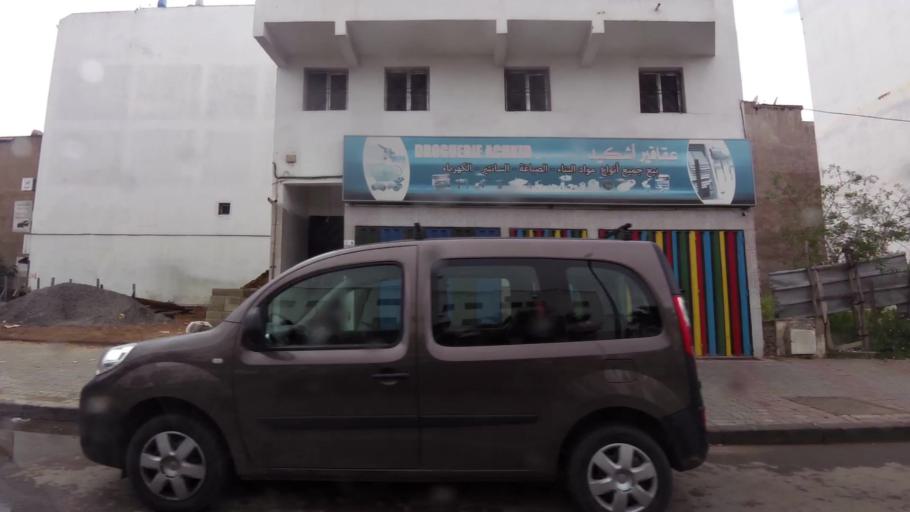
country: MA
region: Grand Casablanca
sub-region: Casablanca
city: Casablanca
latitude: 33.5430
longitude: -7.6847
